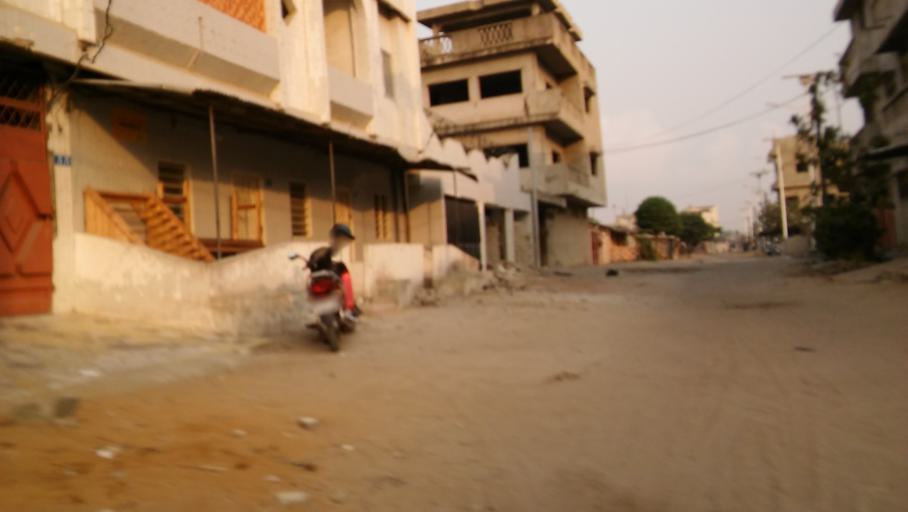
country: BJ
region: Littoral
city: Cotonou
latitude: 6.3909
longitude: 2.3814
